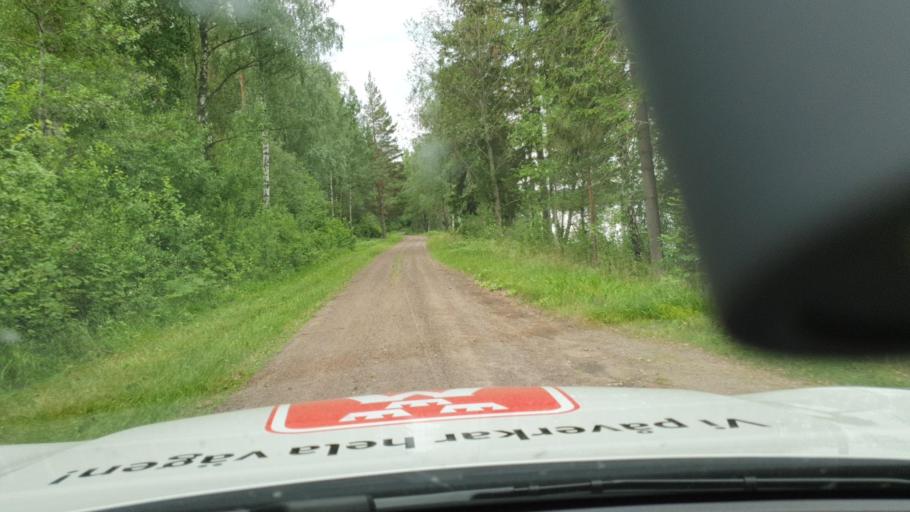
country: SE
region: OErebro
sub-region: Laxa Kommun
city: Laxa
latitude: 58.8275
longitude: 14.5447
